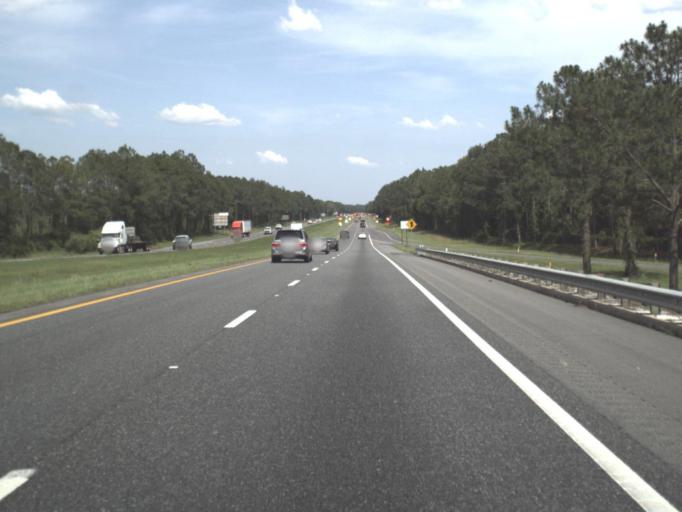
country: US
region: Florida
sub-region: Columbia County
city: Five Points
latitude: 30.2415
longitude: -82.6367
